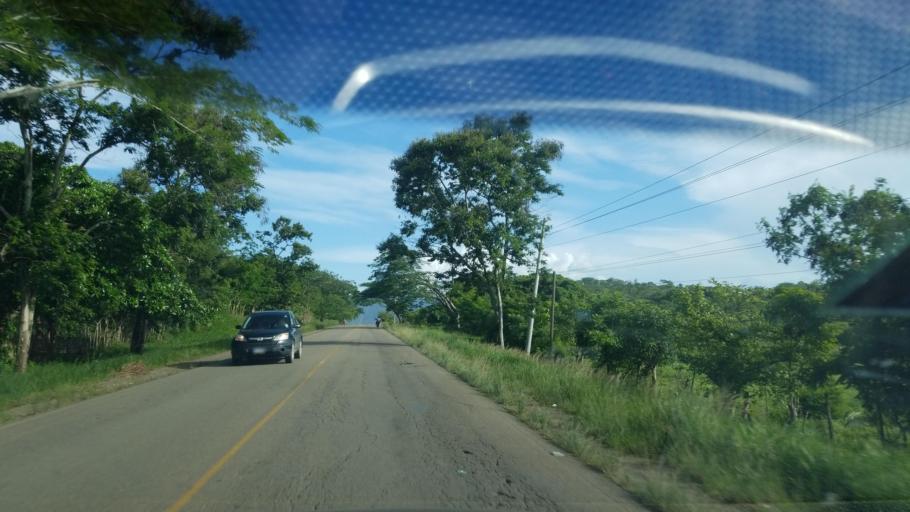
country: HN
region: El Paraiso
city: Arauli
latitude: 13.9194
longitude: -86.5576
